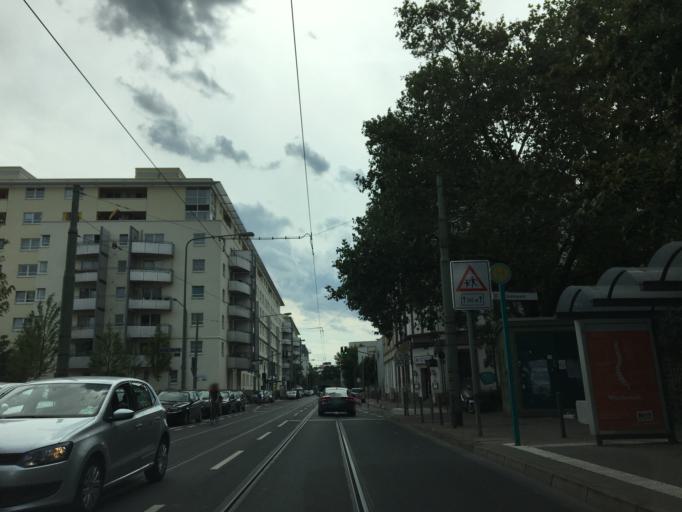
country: DE
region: Hesse
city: Niederrad
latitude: 50.1004
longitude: 8.6375
